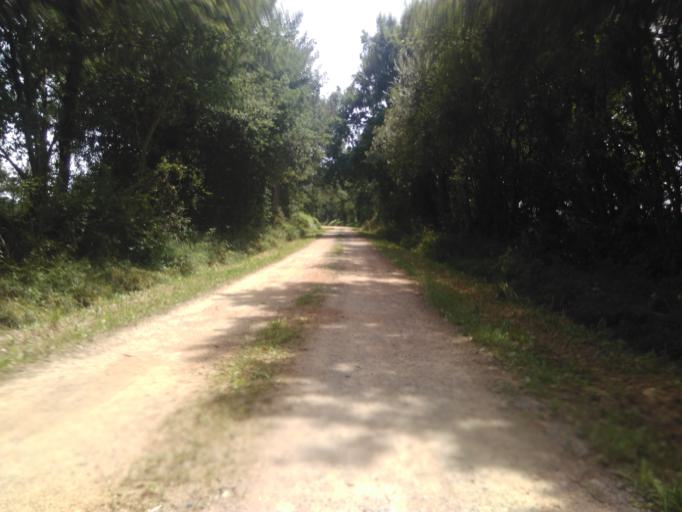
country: FR
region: Pays de la Loire
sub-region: Departement de la Vendee
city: La Ferriere
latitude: 46.7091
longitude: -1.2956
